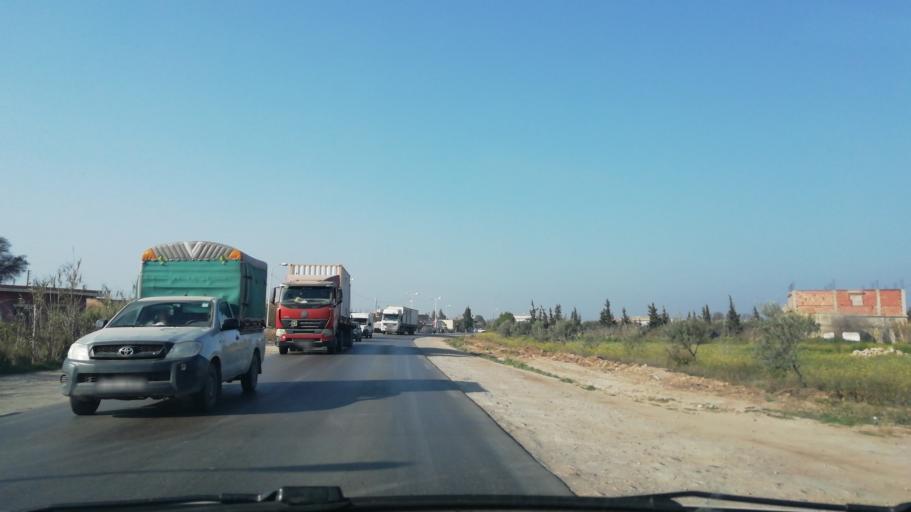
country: DZ
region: Mostaganem
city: Mostaganem
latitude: 35.7570
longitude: 0.0577
